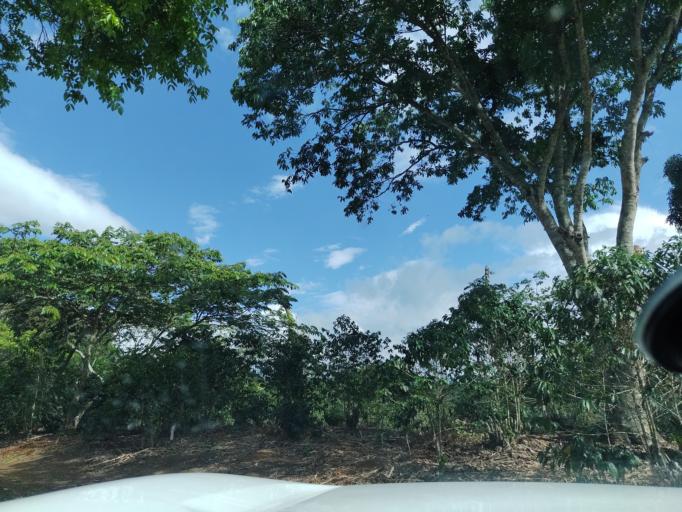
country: MX
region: Veracruz
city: Coatepec
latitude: 19.4851
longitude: -96.9310
